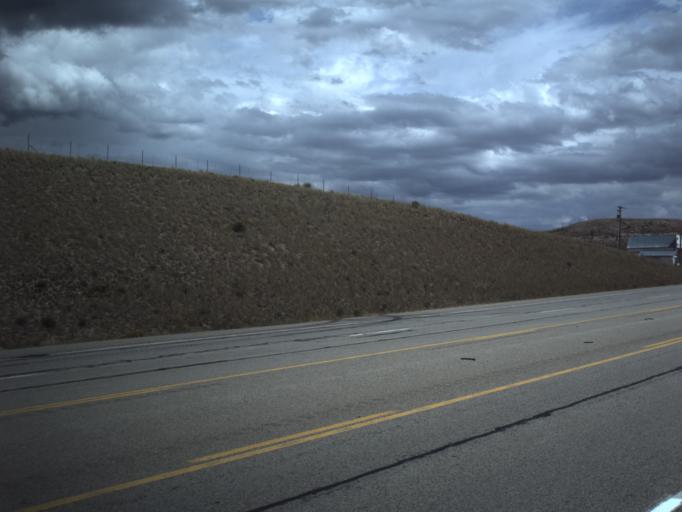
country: US
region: Utah
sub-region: Carbon County
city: Helper
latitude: 39.8502
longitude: -111.0100
